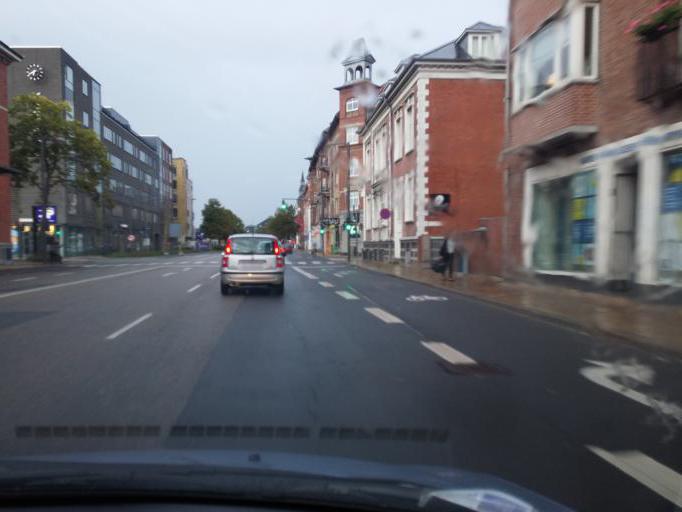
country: DK
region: South Denmark
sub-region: Odense Kommune
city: Odense
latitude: 55.3991
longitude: 10.3798
